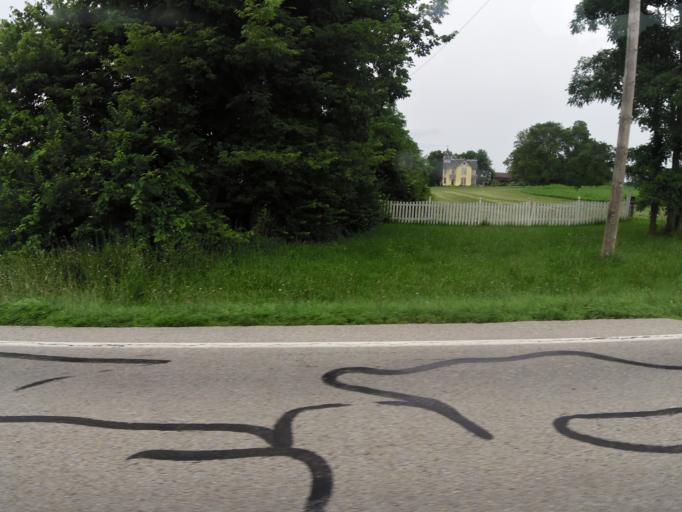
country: US
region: Ohio
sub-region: Warren County
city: Waynesville
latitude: 39.4947
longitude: -83.9737
